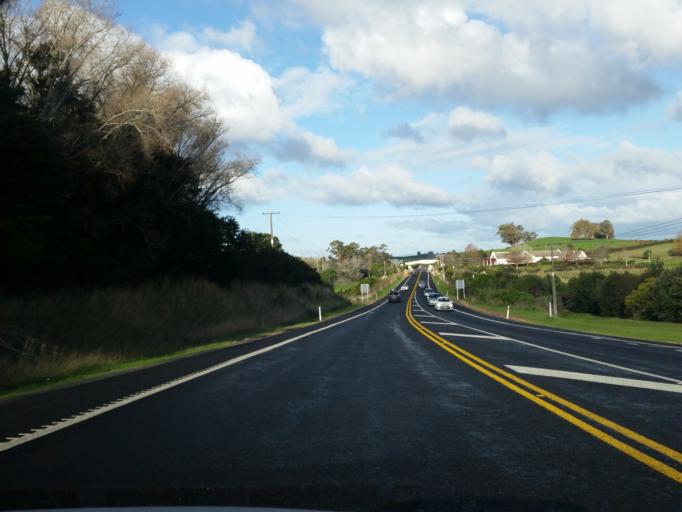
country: NZ
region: Bay of Plenty
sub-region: Western Bay of Plenty District
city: Katikati
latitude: -37.6048
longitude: 175.9378
